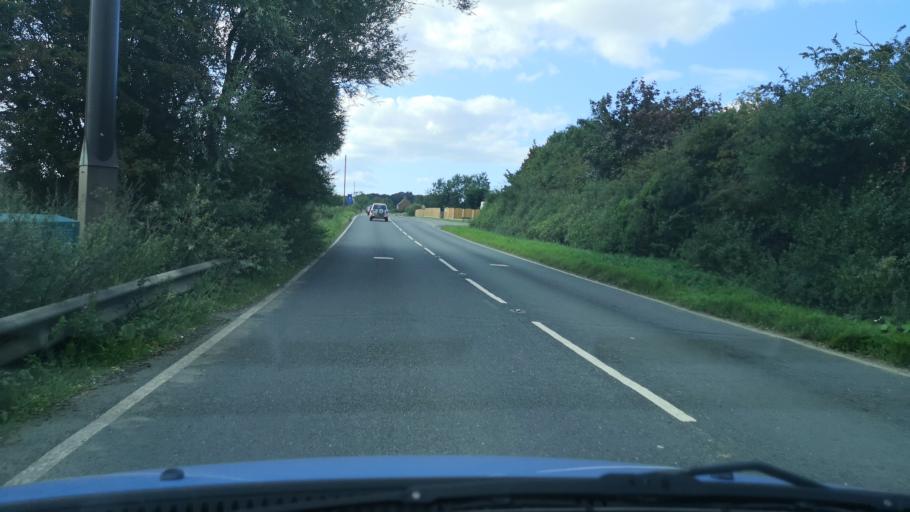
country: GB
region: England
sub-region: City and Borough of Wakefield
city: Upton
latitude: 53.6134
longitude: -1.2953
